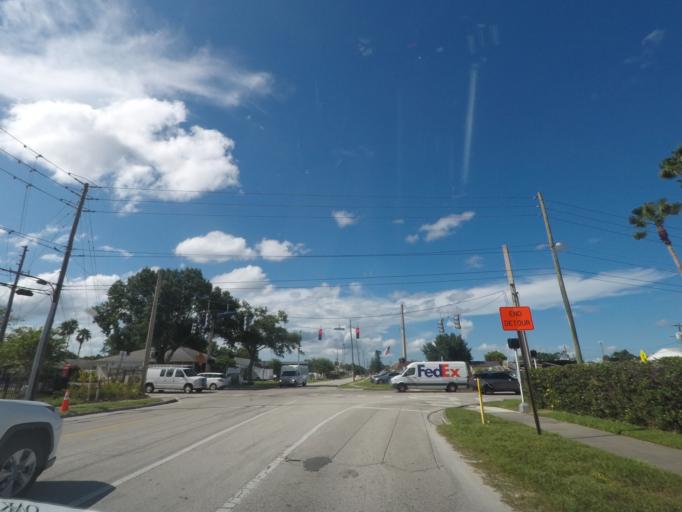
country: US
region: Florida
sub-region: Orange County
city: Fairview Shores
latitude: 28.5892
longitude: -81.3732
